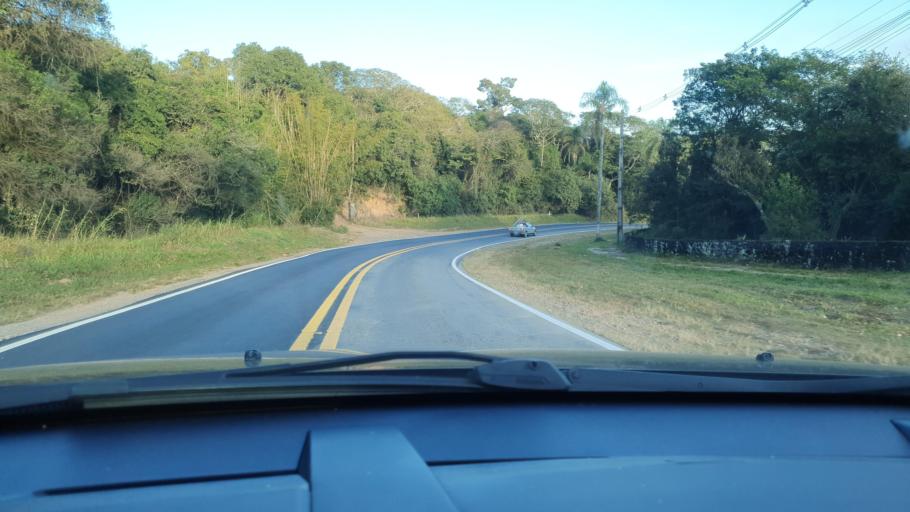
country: BR
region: Sao Paulo
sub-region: Ibiuna
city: Ibiuna
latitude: -23.6765
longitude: -47.3064
